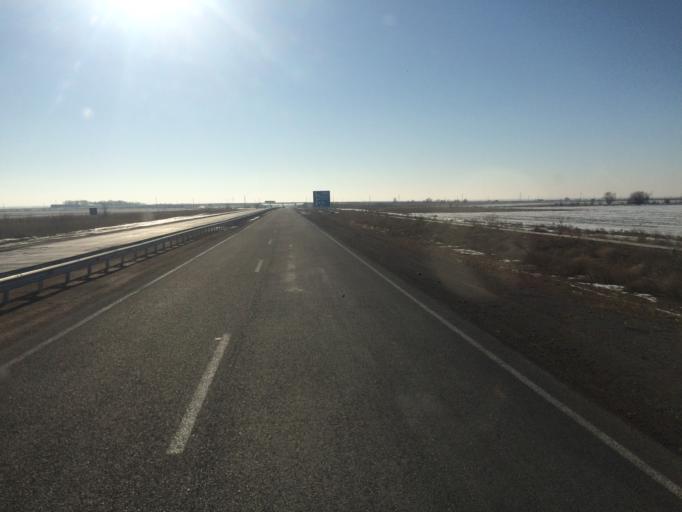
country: KG
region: Chuy
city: Sokuluk
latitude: 43.2839
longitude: 74.2378
